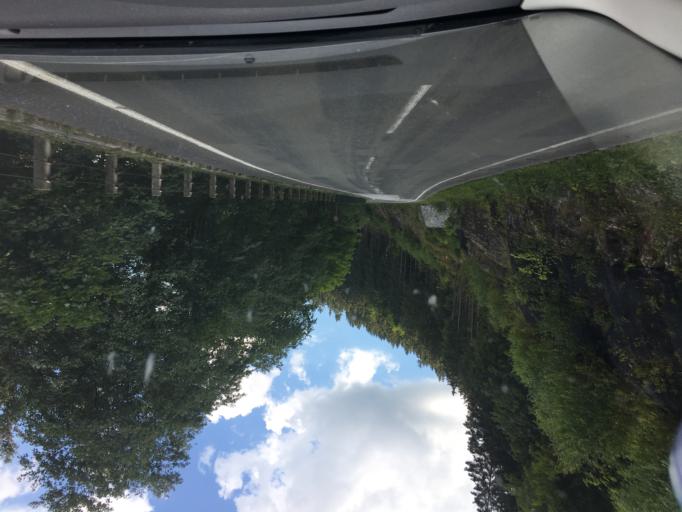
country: CZ
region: Kralovehradecky
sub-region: Okres Trutnov
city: Spindleruv Mlyn
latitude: 50.7054
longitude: 15.5832
